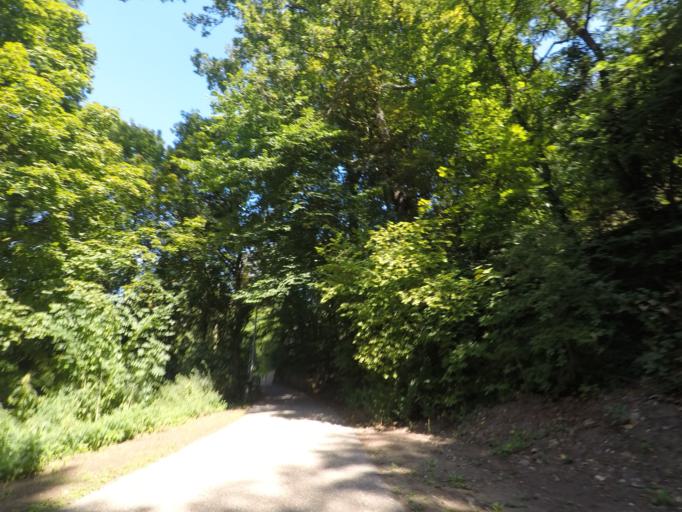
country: LU
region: Luxembourg
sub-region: Canton de Luxembourg
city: Luxembourg
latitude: 49.6225
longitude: 6.1327
